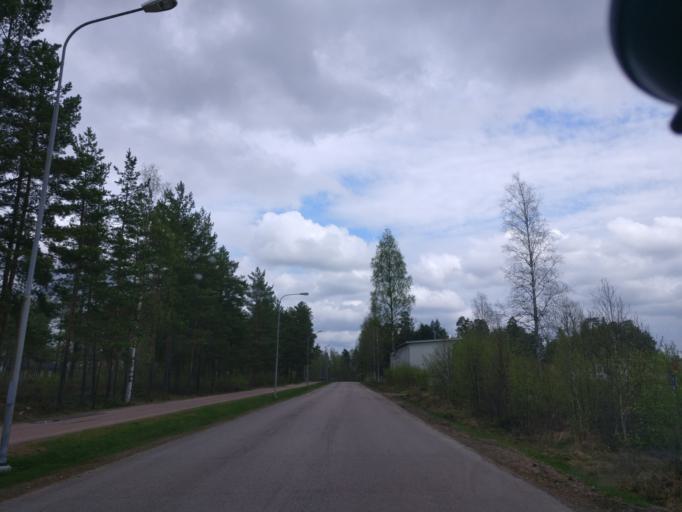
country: SE
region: Vaermland
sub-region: Hagfors Kommun
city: Ekshaerad
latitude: 60.1741
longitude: 13.4865
